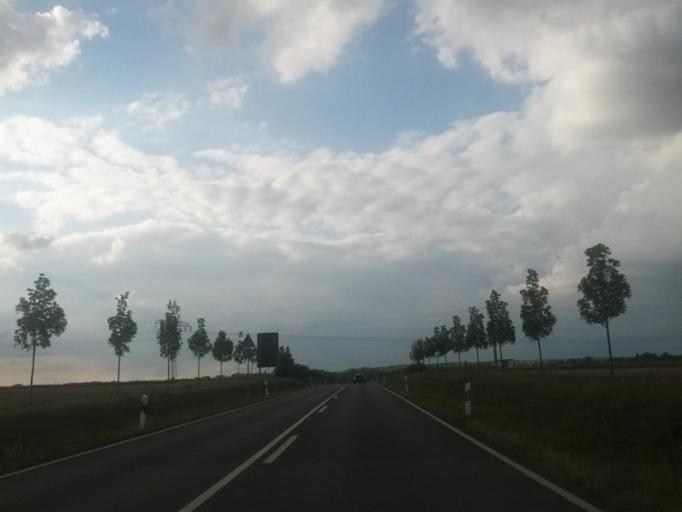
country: DE
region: Thuringia
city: Gotha
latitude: 50.9259
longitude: 10.6899
